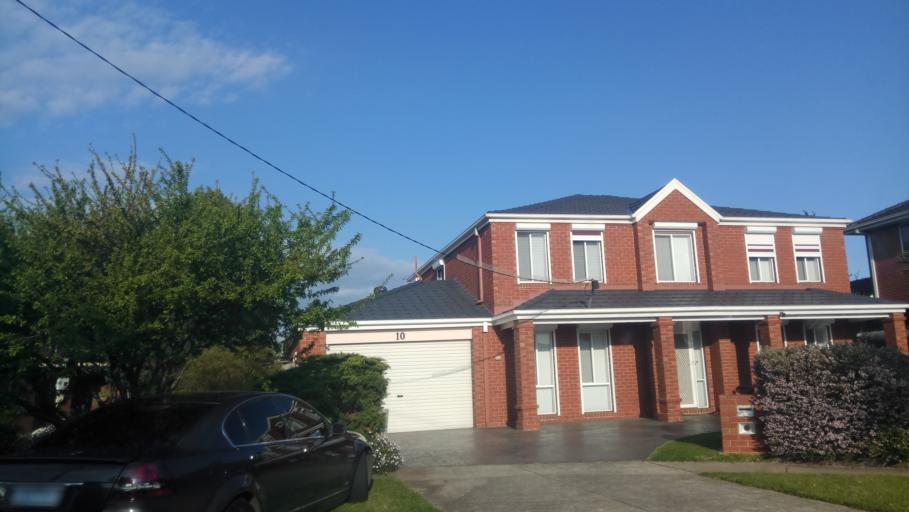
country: AU
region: Victoria
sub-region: Hobsons Bay
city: Altona Meadows
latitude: -37.8833
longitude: 144.7907
